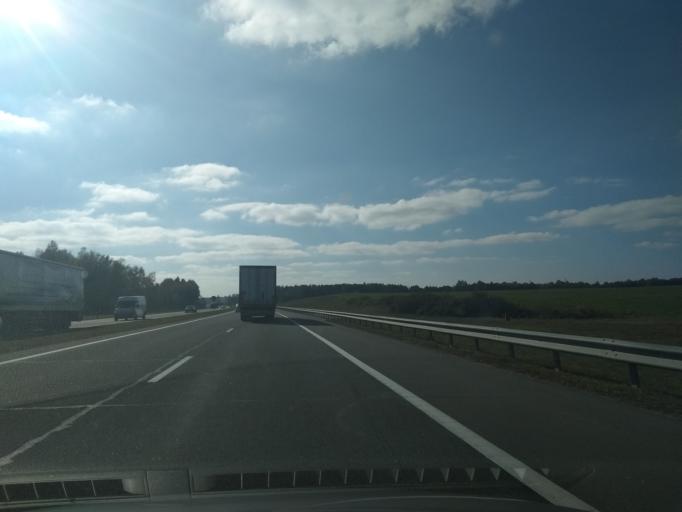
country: BY
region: Brest
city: Baranovichi
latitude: 53.1222
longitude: 25.9015
